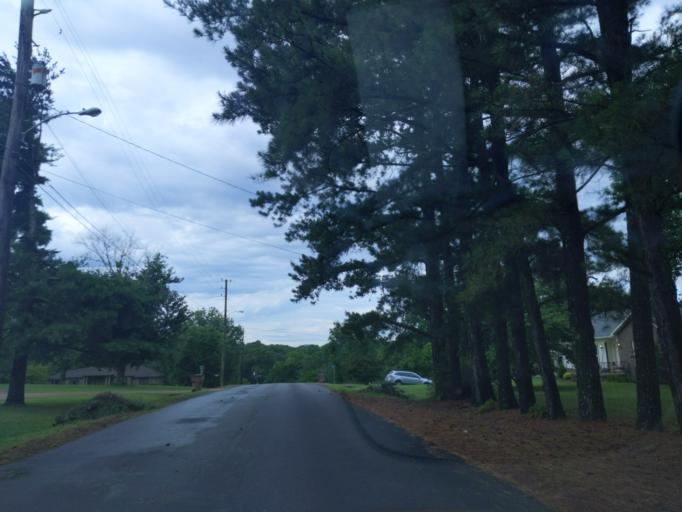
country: US
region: Tennessee
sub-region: Williamson County
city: Brentwood Estates
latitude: 36.0366
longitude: -86.7402
